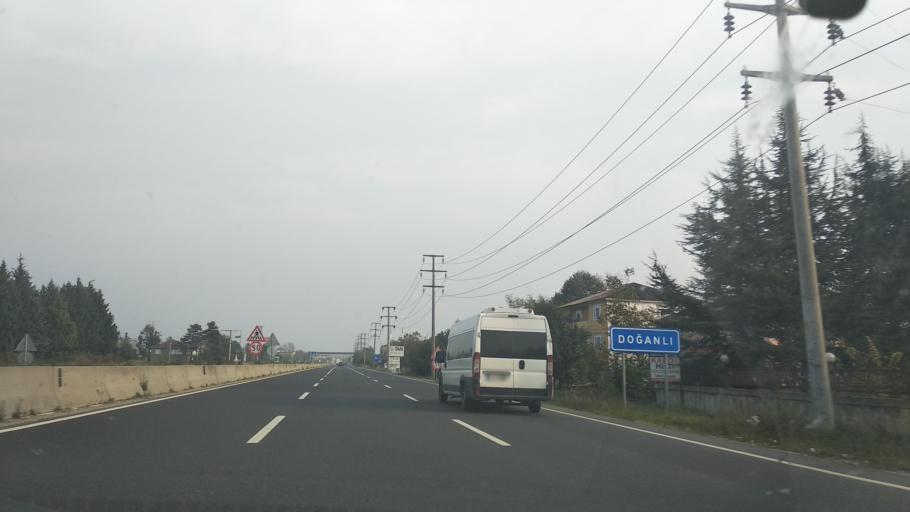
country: TR
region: Duzce
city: Duzce
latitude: 40.8083
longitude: 31.2277
